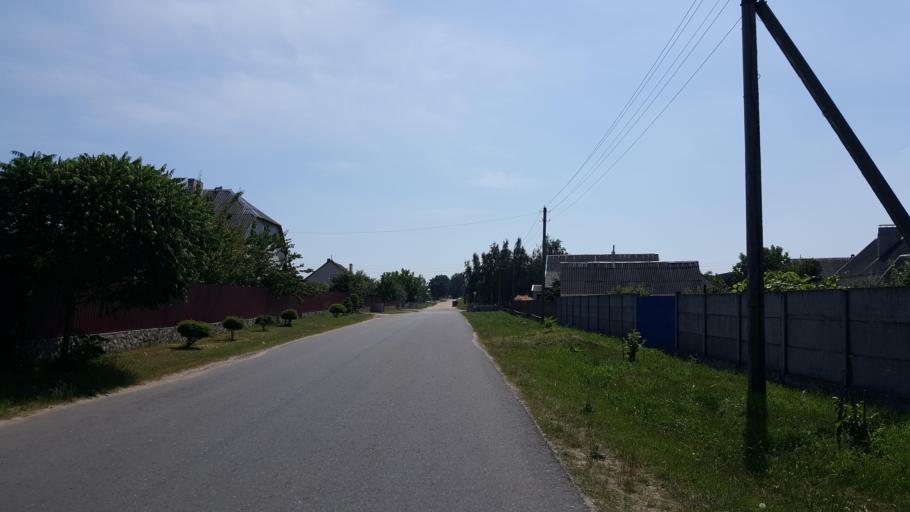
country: BY
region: Brest
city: Kamyanyets
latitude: 52.4018
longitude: 23.8407
